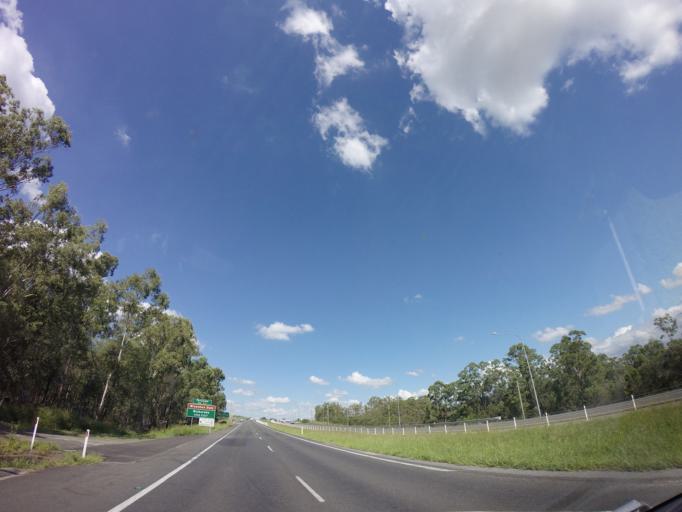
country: AU
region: Queensland
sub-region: Ipswich
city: Brassall
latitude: -27.5770
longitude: 152.6935
